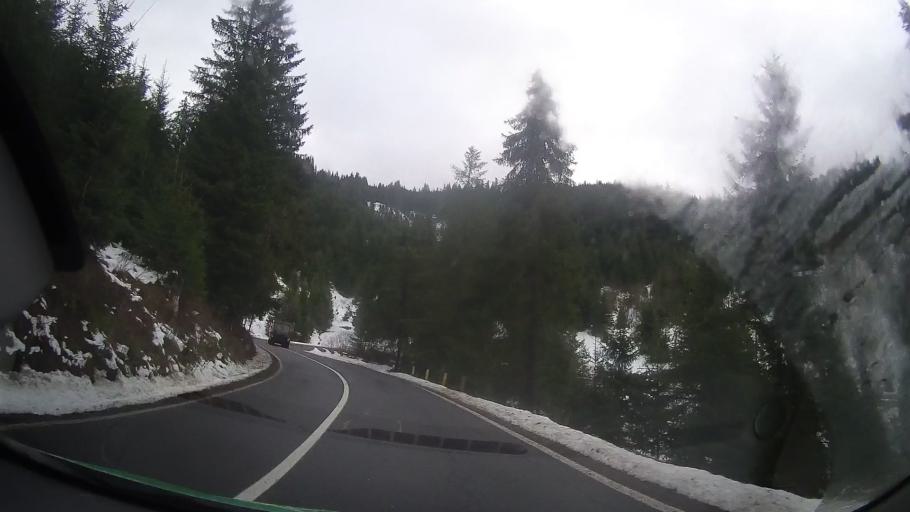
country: RO
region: Harghita
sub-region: Municipiul Gheorgheni
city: Gheorgheni
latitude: 46.7732
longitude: 25.7125
